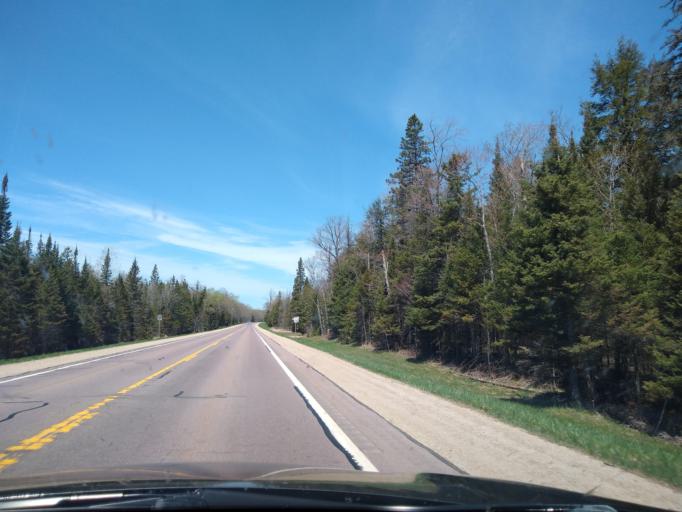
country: US
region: Michigan
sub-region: Marquette County
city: K. I. Sawyer Air Force Base
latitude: 46.2343
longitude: -87.0718
